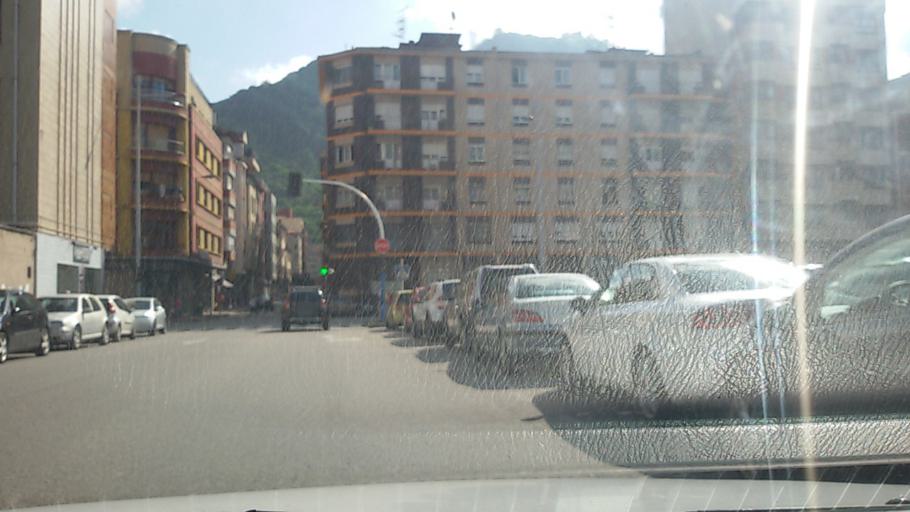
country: ES
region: Asturias
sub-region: Province of Asturias
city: Mieres
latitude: 43.2495
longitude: -5.7768
